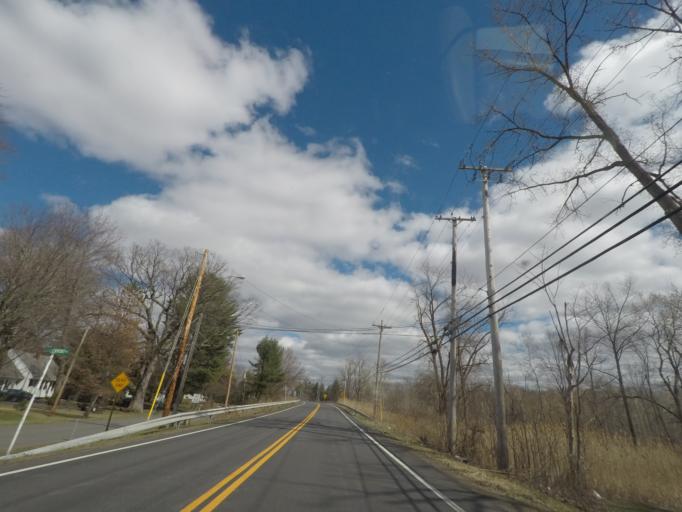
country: US
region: New York
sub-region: Albany County
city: Delmar
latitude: 42.5999
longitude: -73.7875
